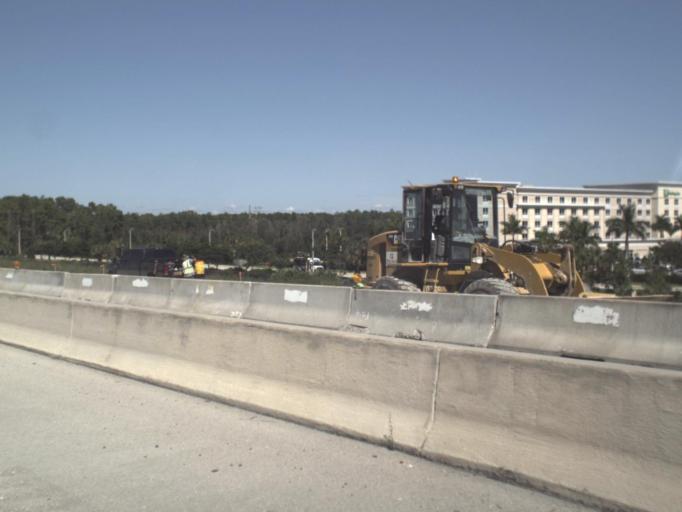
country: US
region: Florida
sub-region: Lee County
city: Three Oaks
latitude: 26.4952
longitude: -81.7942
